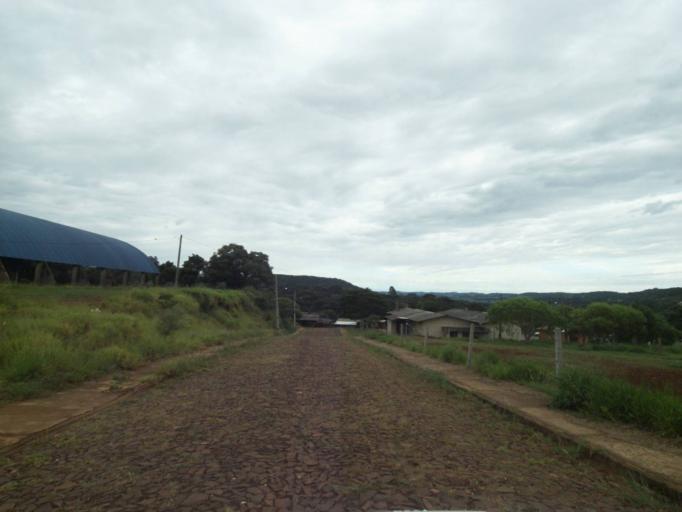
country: BR
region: Parana
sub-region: Guaraniacu
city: Guaraniacu
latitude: -25.1137
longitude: -52.8502
